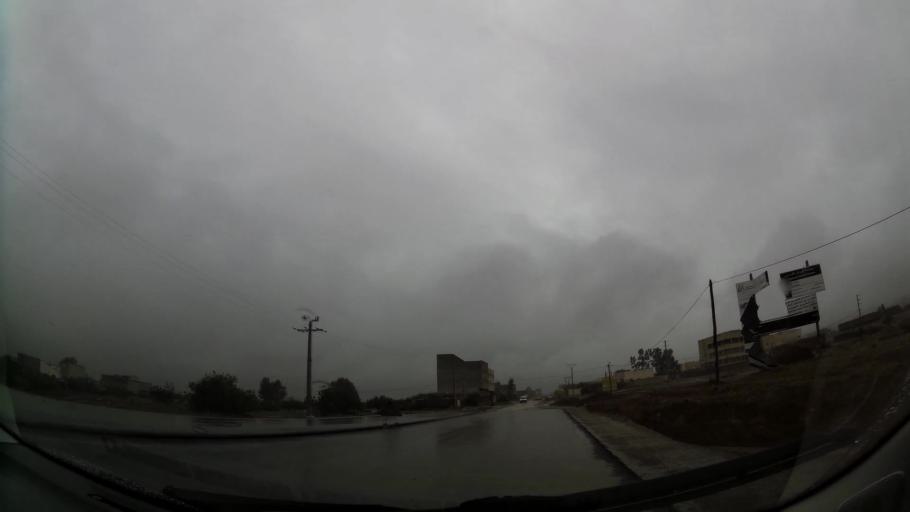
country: MA
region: Oriental
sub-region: Nador
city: Midar
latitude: 34.8781
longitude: -3.7260
